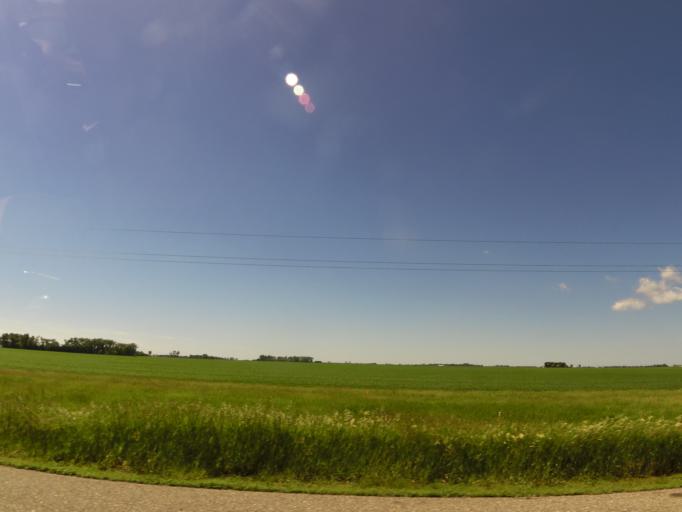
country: US
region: Minnesota
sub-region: Polk County
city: Crookston
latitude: 47.7603
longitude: -96.5119
